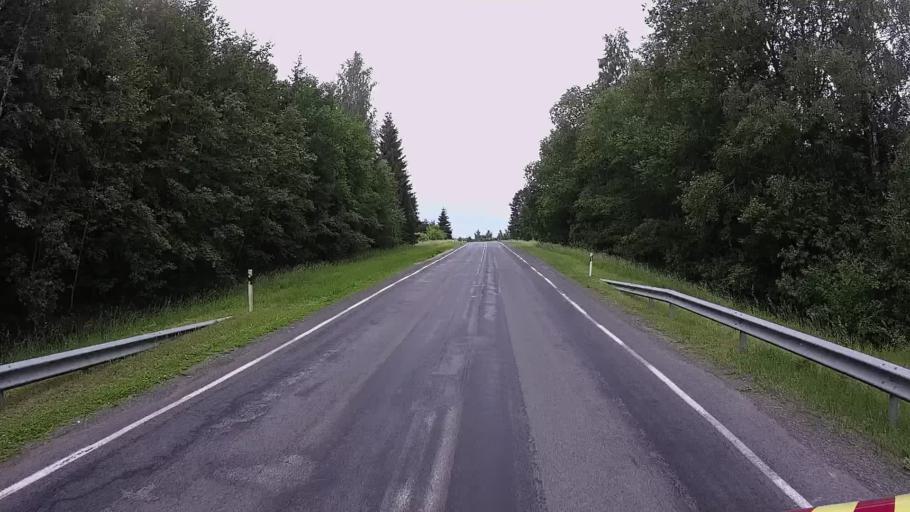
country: EE
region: Viljandimaa
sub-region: Karksi vald
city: Karksi-Nuia
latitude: 58.1849
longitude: 25.5966
